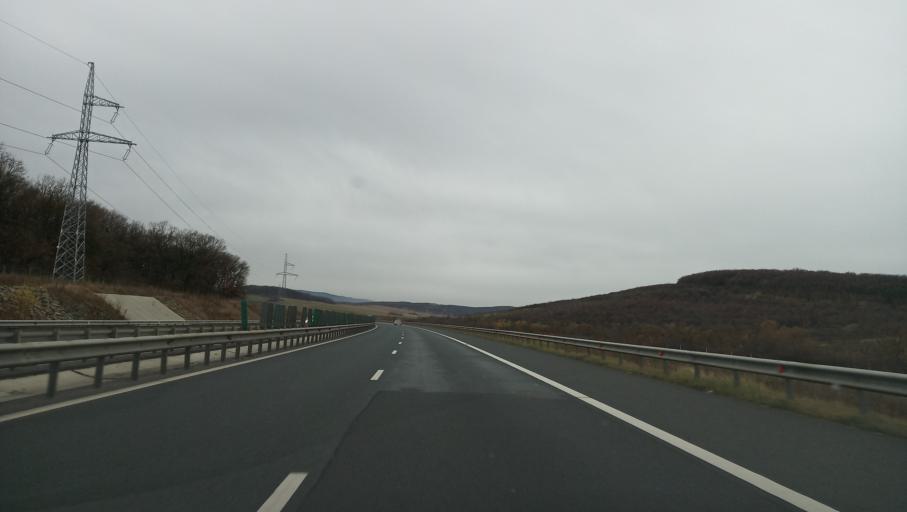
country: RO
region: Sibiu
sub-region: Comuna Cristian
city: Cristian
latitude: 45.8019
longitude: 24.0408
